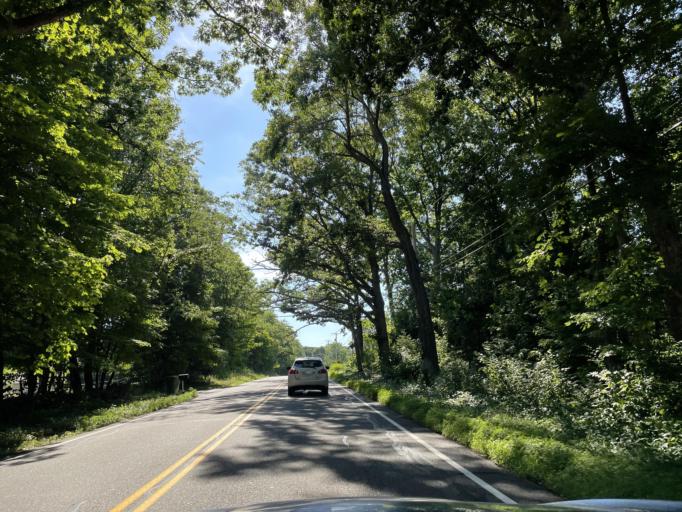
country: US
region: Massachusetts
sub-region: Worcester County
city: Sutton
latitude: 42.1517
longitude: -71.7079
